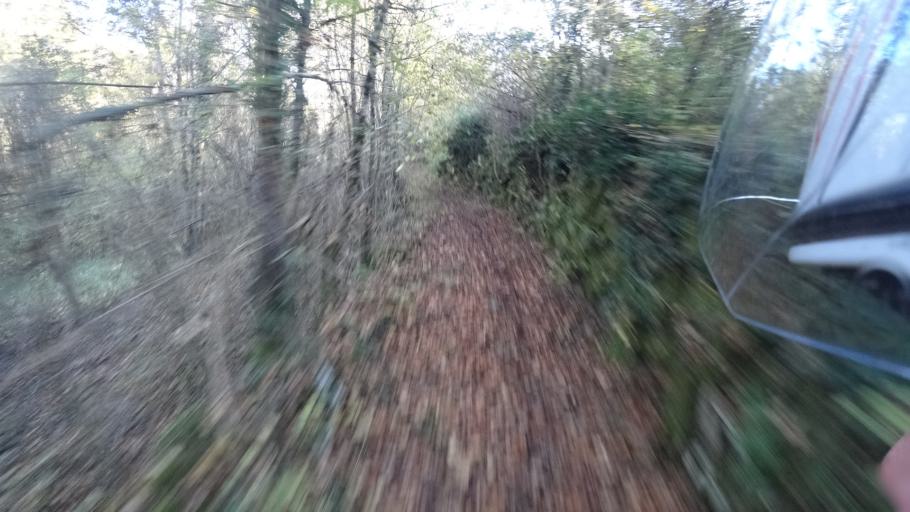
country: HR
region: Primorsko-Goranska
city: Matulji
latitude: 45.4062
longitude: 14.2850
